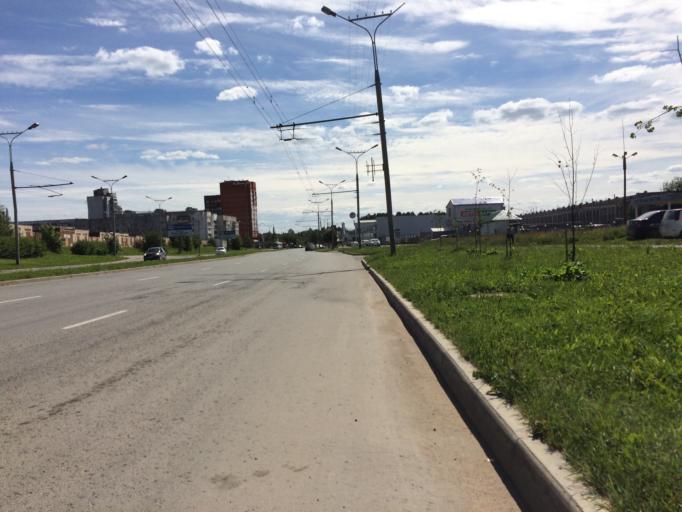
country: RU
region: Mariy-El
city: Yoshkar-Ola
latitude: 56.6281
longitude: 47.9359
